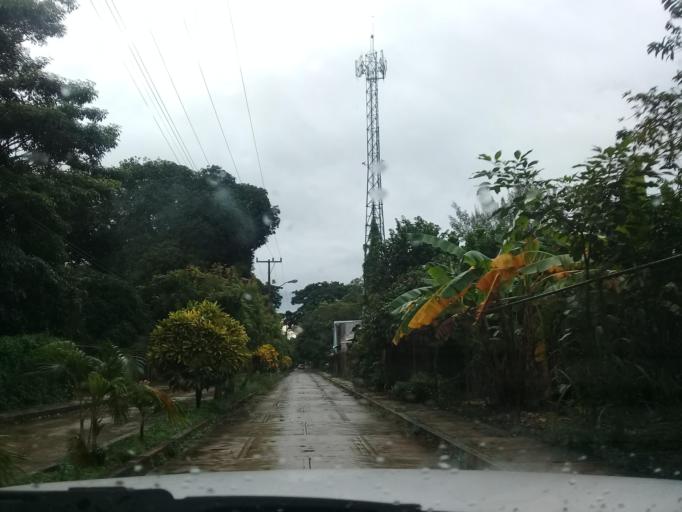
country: MX
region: Veracruz
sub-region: San Andres Tuxtla
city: Cerro las Iguanas
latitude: 18.4245
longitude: -95.2183
